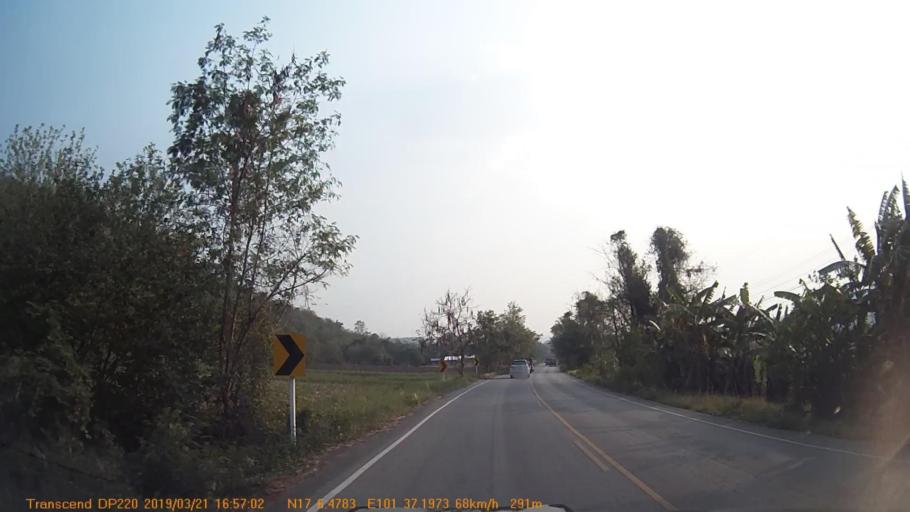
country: TH
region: Loei
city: Phu Luang
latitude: 17.1078
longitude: 101.6199
